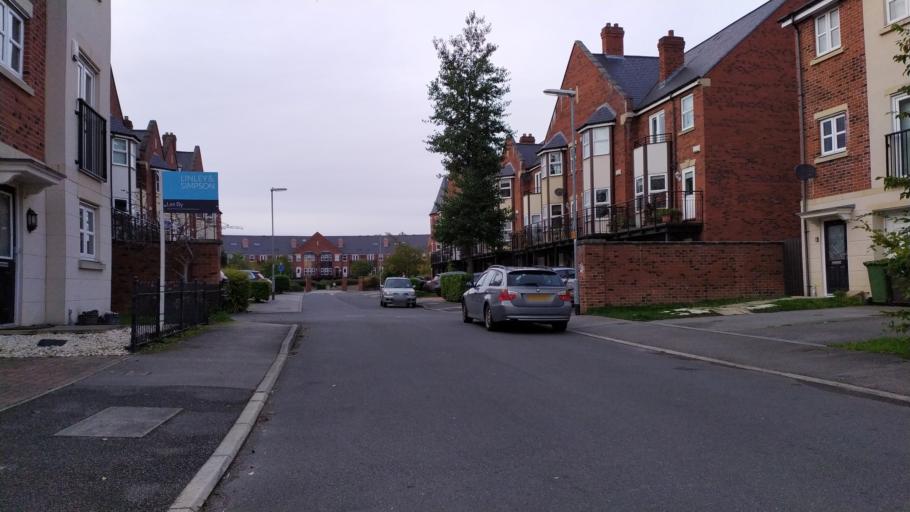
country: GB
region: England
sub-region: City and Borough of Leeds
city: Horsforth
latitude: 53.8296
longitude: -1.5903
